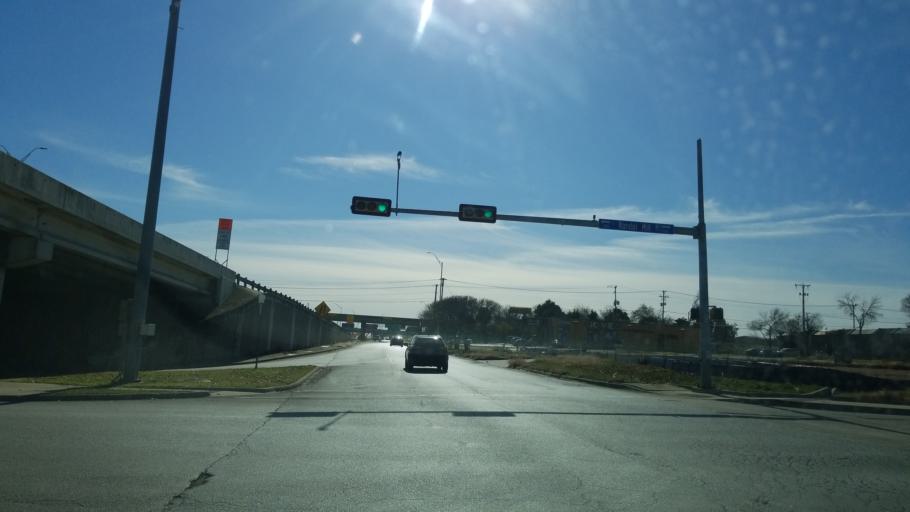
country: US
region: Texas
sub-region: Tarrant County
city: Arlington
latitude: 32.7489
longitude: -97.0631
